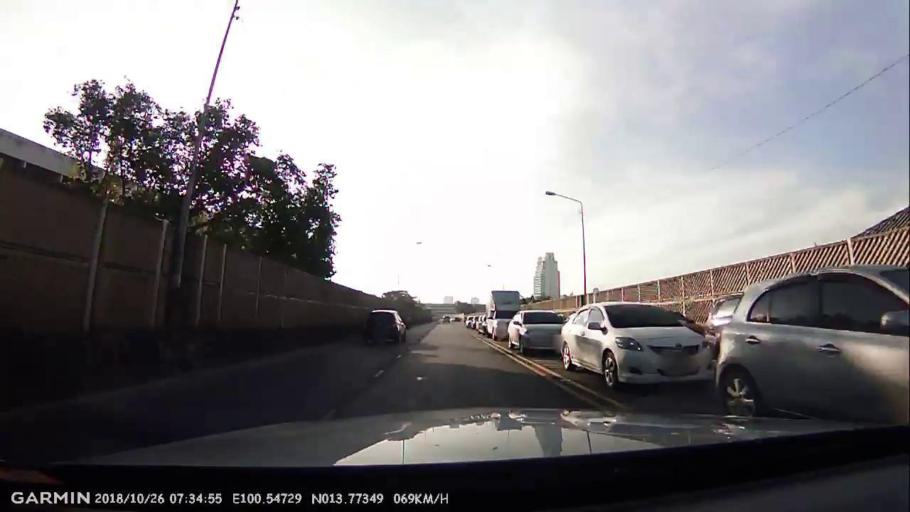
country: TH
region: Bangkok
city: Din Daeng
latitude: 13.7734
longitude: 100.5474
